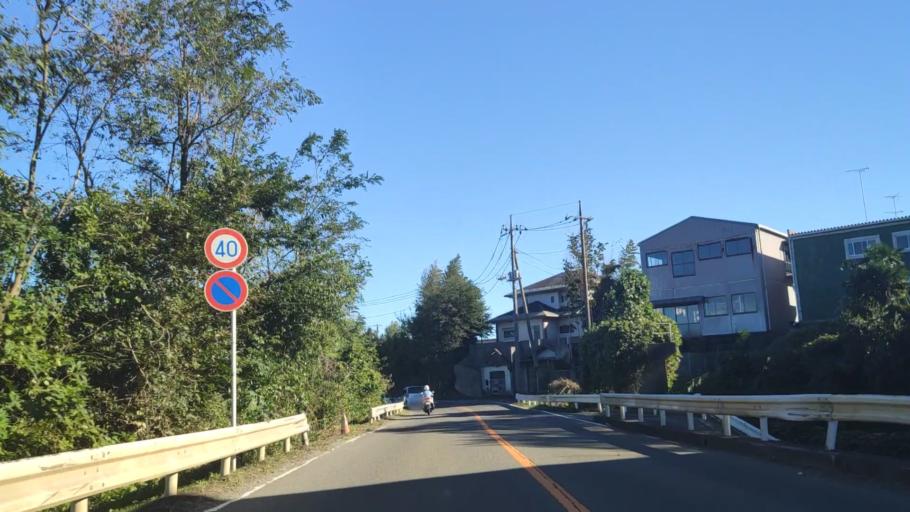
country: JP
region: Kanagawa
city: Zama
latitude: 35.5194
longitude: 139.3621
